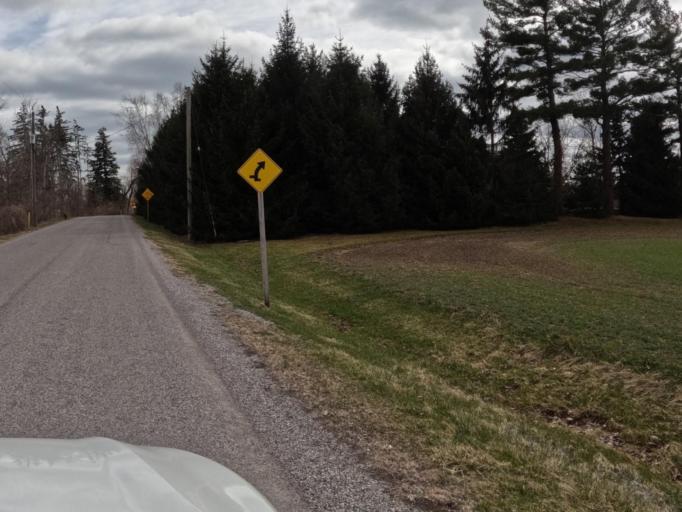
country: CA
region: Ontario
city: Norfolk County
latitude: 42.8013
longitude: -80.2137
